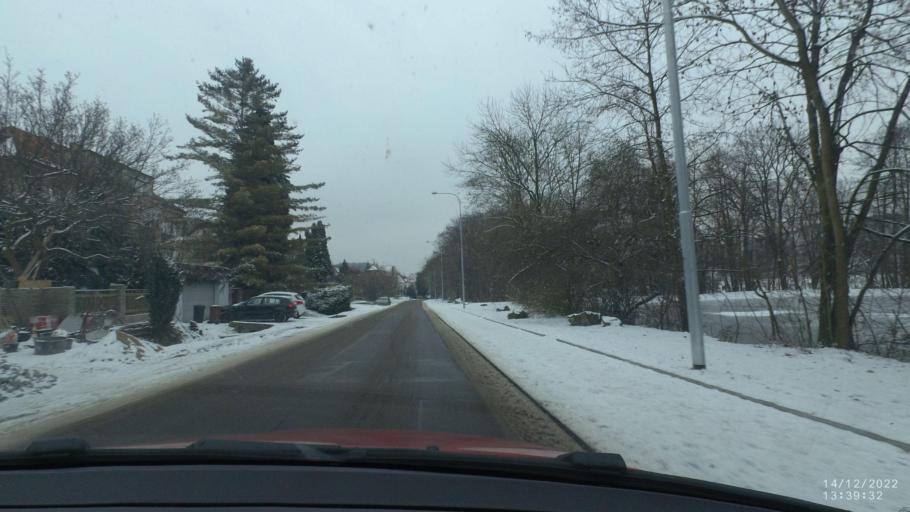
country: CZ
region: Central Bohemia
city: Horomerice
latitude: 50.0696
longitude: 14.3403
